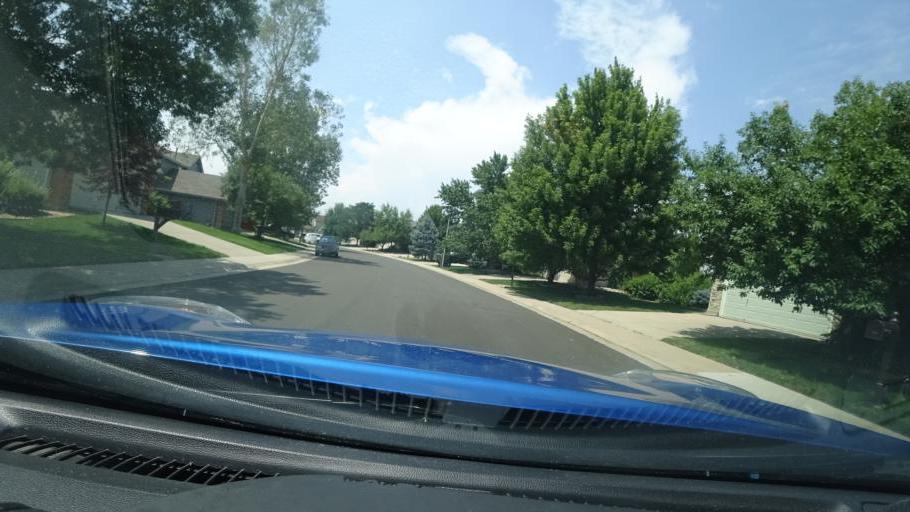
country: US
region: Colorado
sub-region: Adams County
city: Aurora
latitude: 39.6663
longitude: -104.7683
